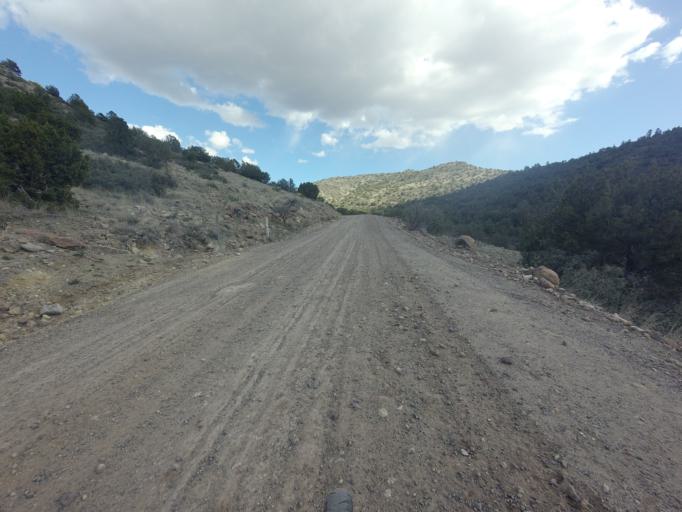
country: US
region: Arizona
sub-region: Yavapai County
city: Camp Verde
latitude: 34.4266
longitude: -111.6857
